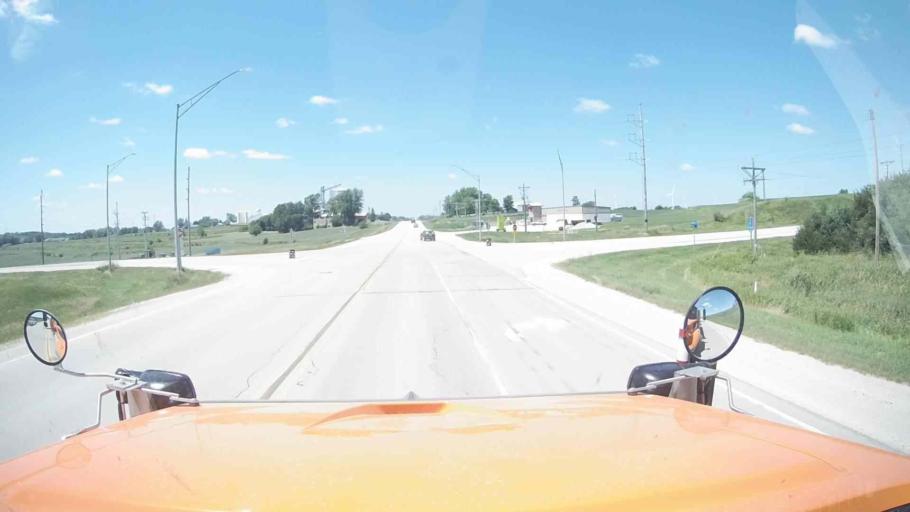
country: US
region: Iowa
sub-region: Adams County
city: Corning
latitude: 41.2584
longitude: -94.7572
